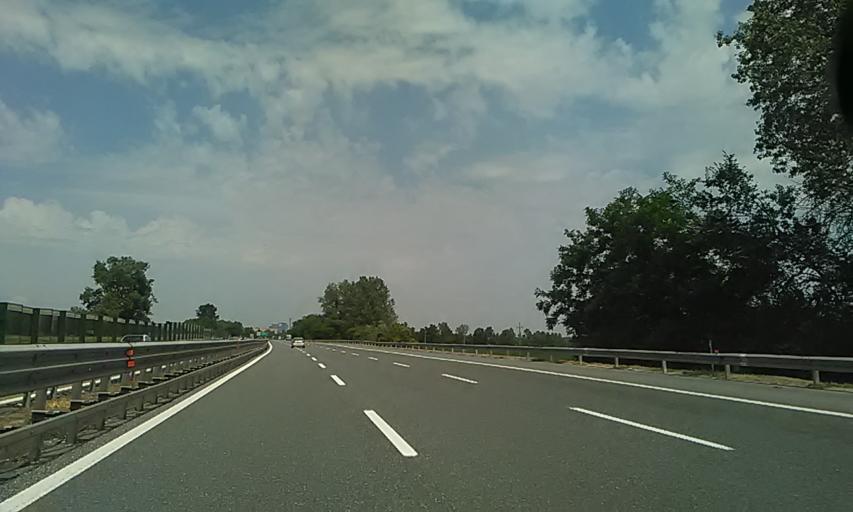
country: IT
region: Piedmont
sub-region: Provincia di Alessandria
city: Silvano d'Orba
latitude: 44.7073
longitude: 8.6676
